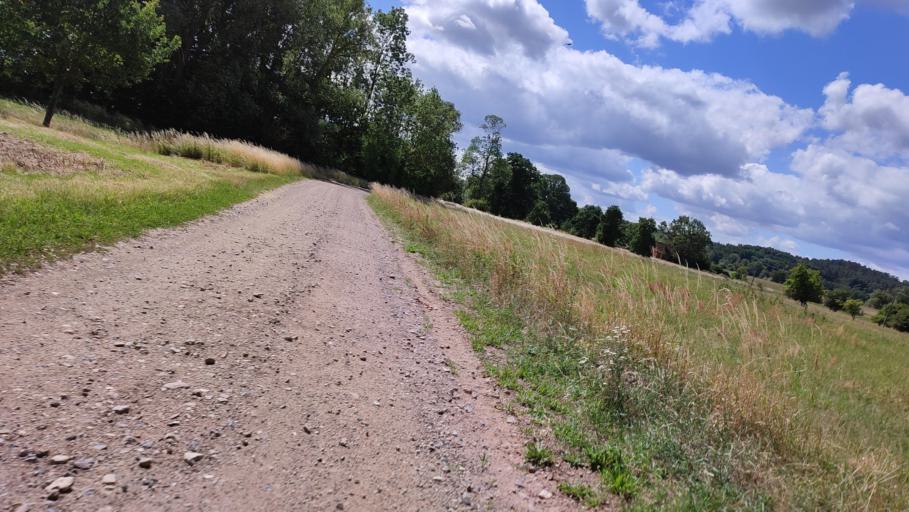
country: DE
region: Lower Saxony
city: Hitzacker
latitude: 53.2000
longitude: 10.9830
